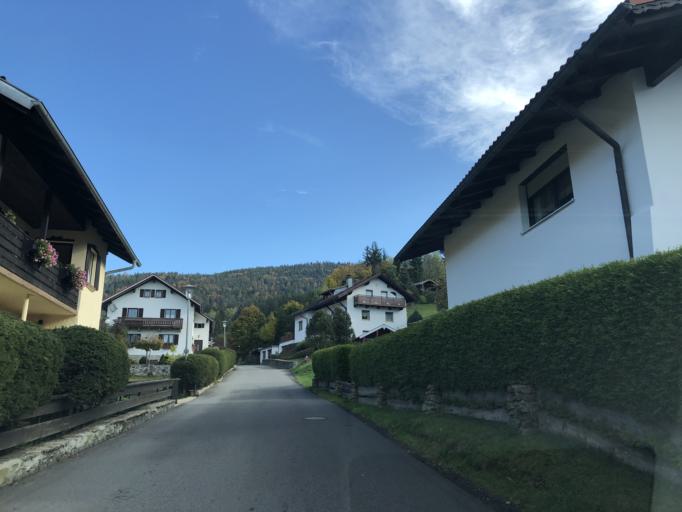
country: DE
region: Bavaria
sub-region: Lower Bavaria
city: Bodenmais
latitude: 49.0735
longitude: 13.1053
